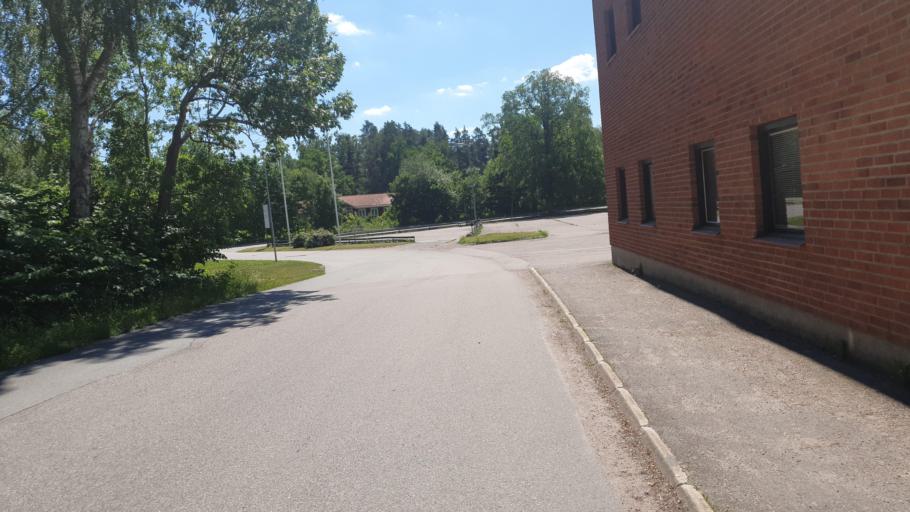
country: SE
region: Uppsala
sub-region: Osthammars Kommun
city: Gimo
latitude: 60.1761
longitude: 18.1774
